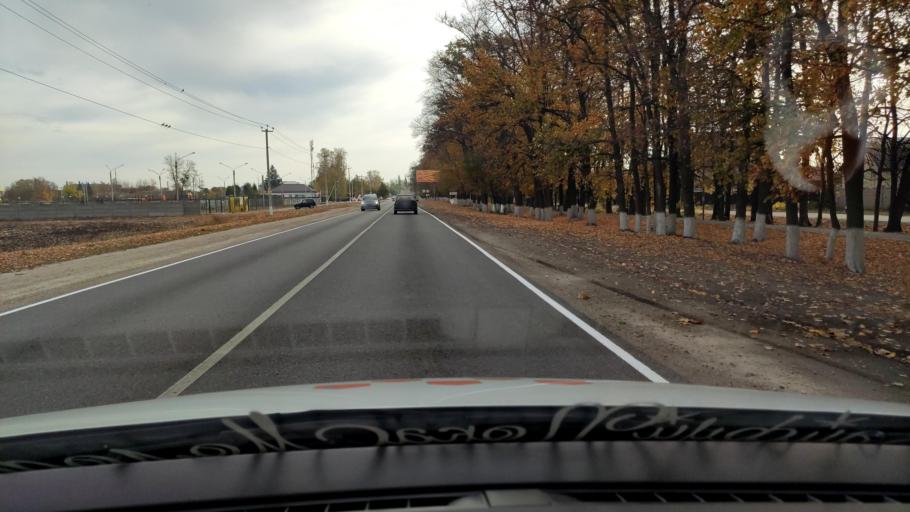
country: RU
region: Voronezj
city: Ramon'
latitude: 51.9117
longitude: 39.3247
